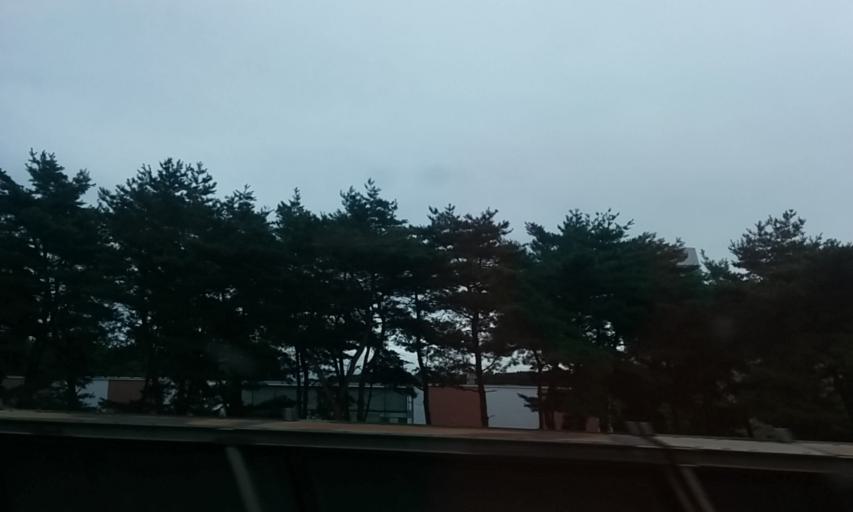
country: JP
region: Tochigi
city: Mibu
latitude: 36.4023
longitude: 139.8584
